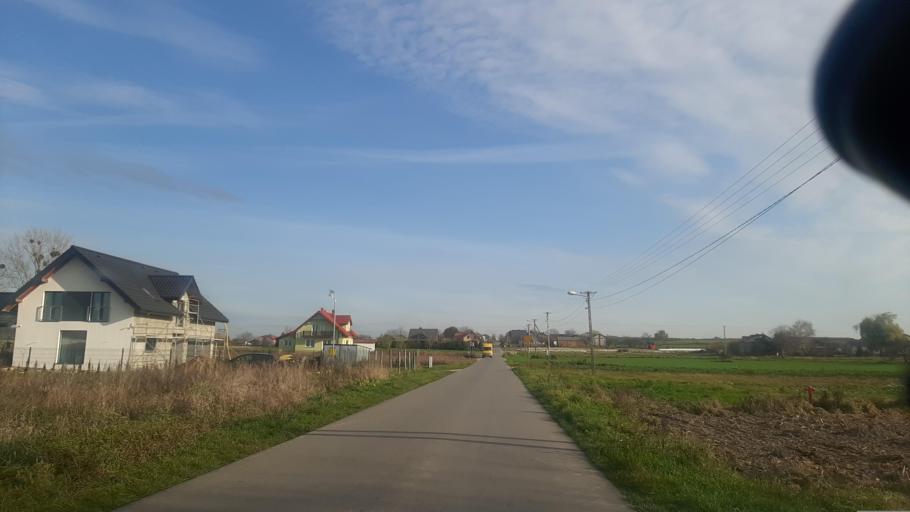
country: PL
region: Lublin Voivodeship
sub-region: Powiat lubelski
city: Garbow
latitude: 51.3903
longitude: 22.3275
